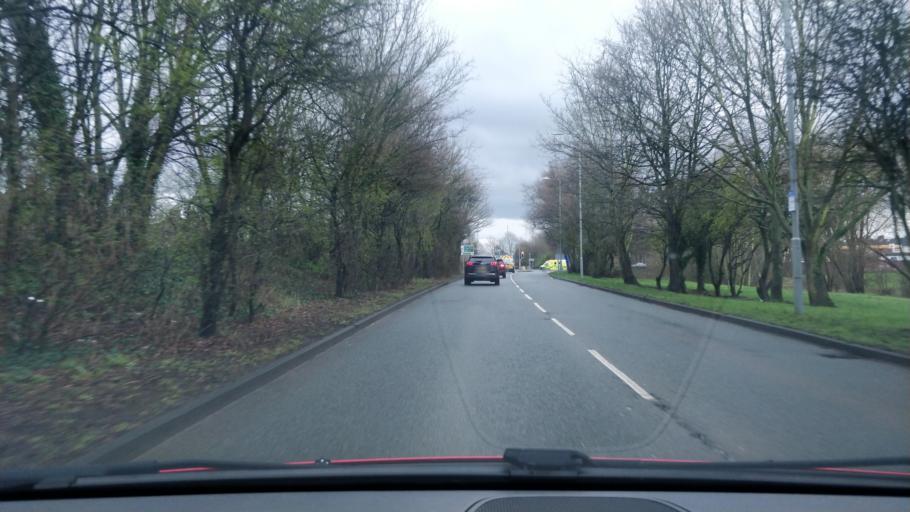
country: GB
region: England
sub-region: Knowsley
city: Huyton
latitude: 53.4222
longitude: -2.8487
